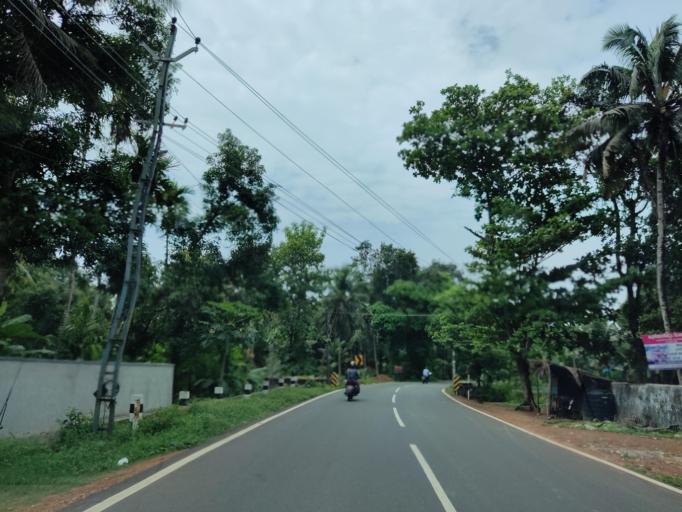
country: IN
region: Kerala
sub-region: Alappuzha
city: Mavelikara
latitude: 9.2677
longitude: 76.6008
